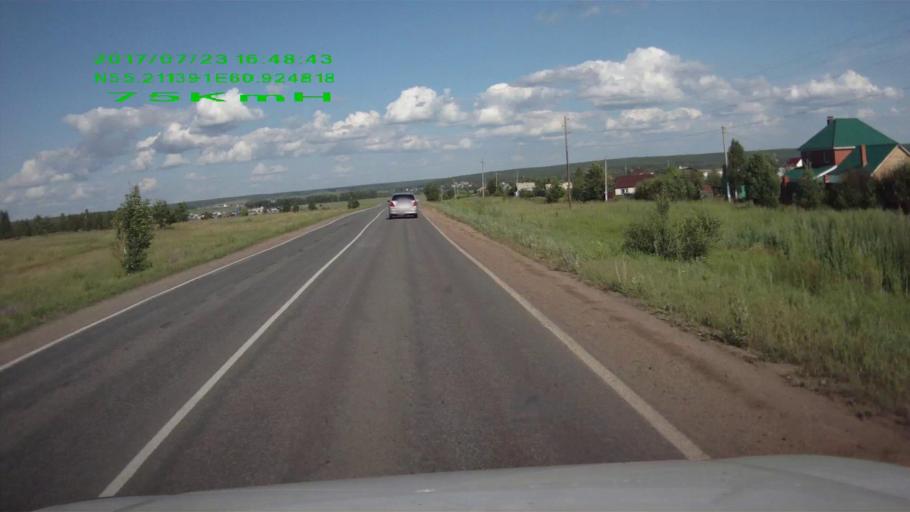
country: RU
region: Chelyabinsk
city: Poletayevo
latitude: 55.2114
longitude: 60.9246
